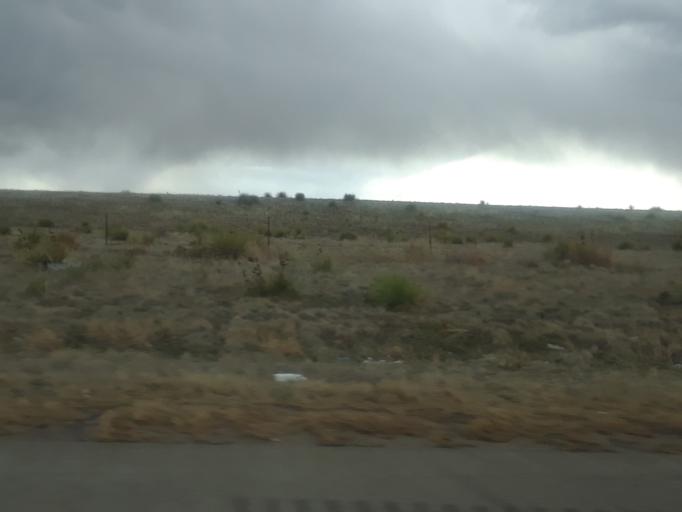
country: US
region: Colorado
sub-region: Arapahoe County
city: Byers
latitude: 39.6611
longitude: -104.0833
